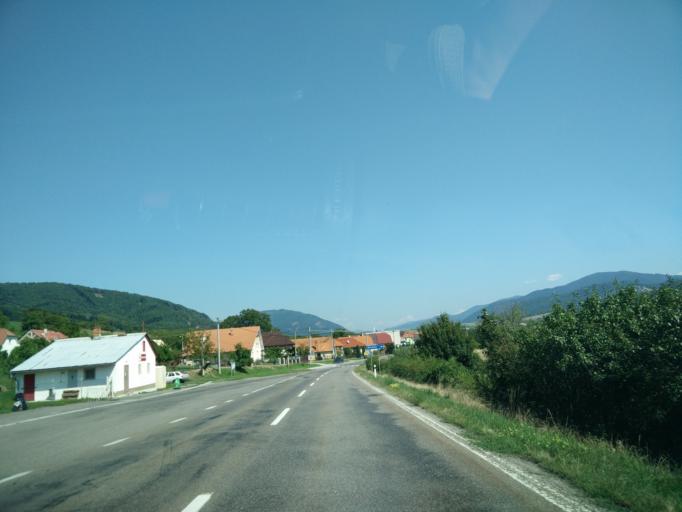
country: SK
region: Banskobystricky
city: Nova Bana
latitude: 48.3833
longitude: 18.6010
